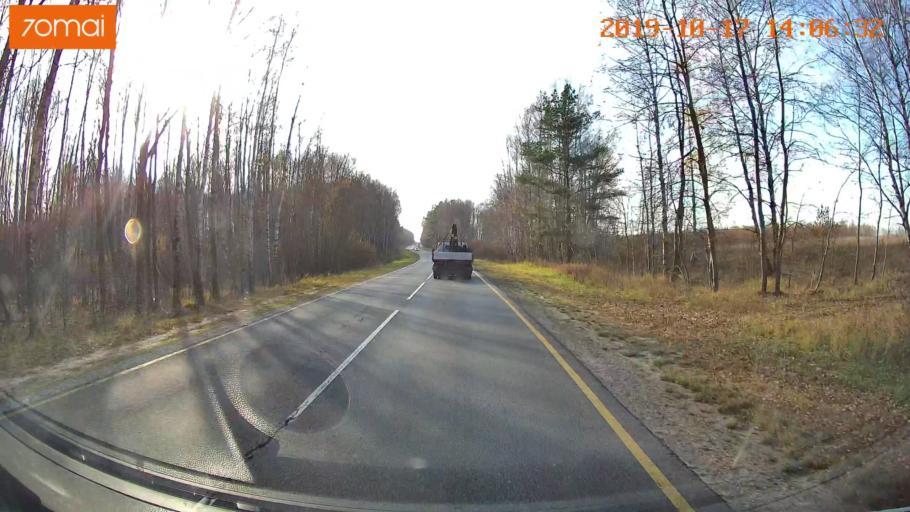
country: RU
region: Rjazan
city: Spas-Klepiki
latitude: 55.1124
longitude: 40.1043
